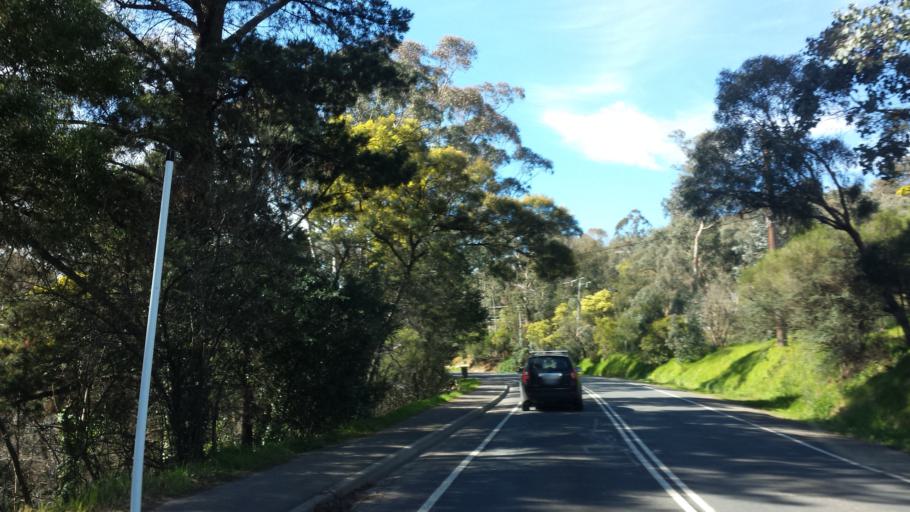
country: AU
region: Victoria
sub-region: Nillumbik
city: North Warrandyte
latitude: -37.7345
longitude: 145.2232
